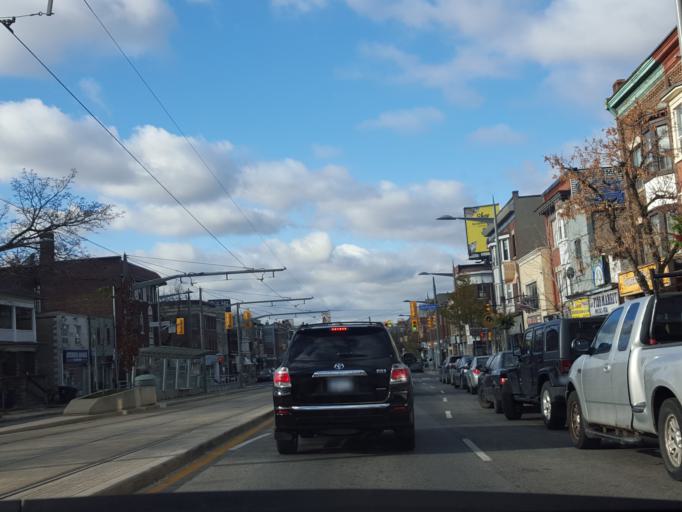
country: CA
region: Ontario
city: Toronto
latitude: 43.6792
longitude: -79.4376
